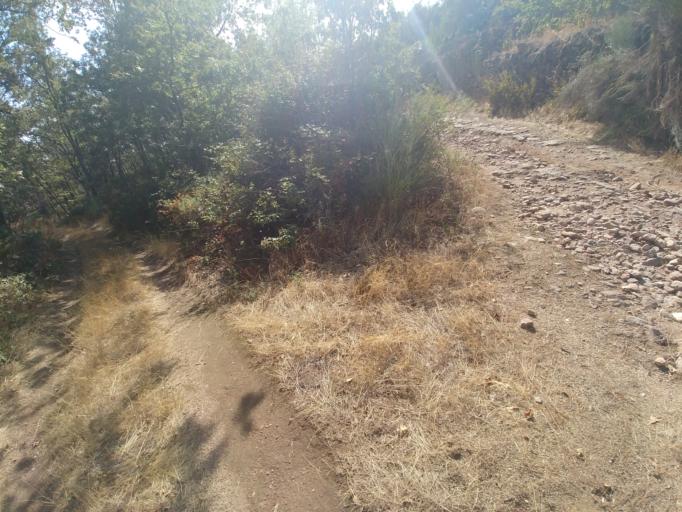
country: ES
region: Extremadura
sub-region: Provincia de Caceres
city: Garganta la Olla
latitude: 40.0966
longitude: -5.7519
